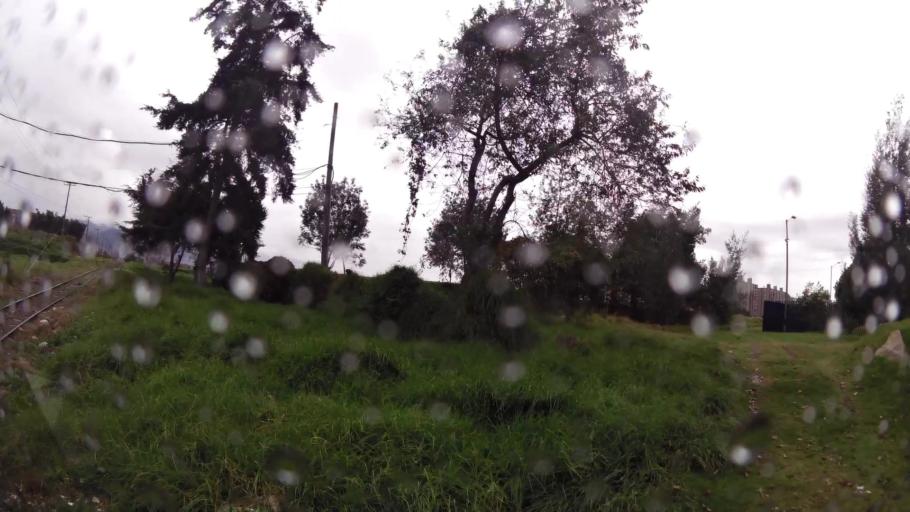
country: CO
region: Bogota D.C.
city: Bogota
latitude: 4.6615
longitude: -74.1262
